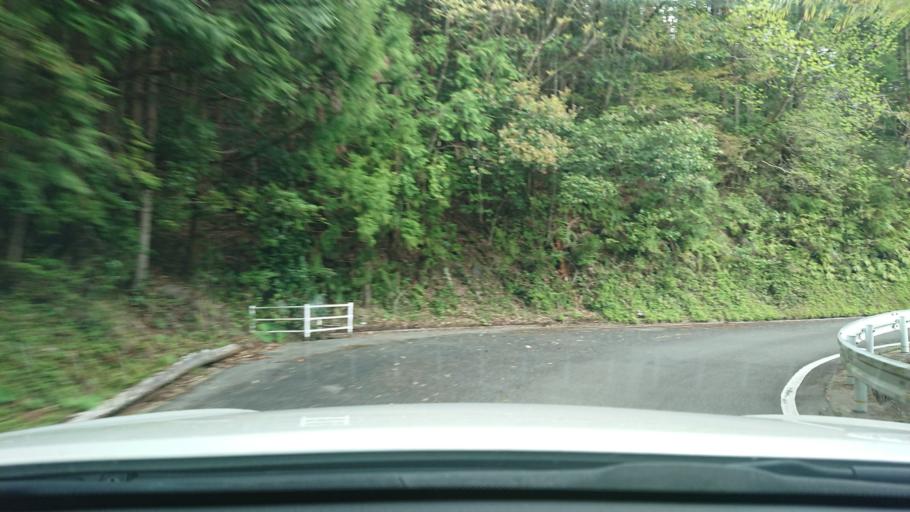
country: JP
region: Tokushima
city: Kamojimacho-jogejima
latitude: 33.8848
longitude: 134.3849
